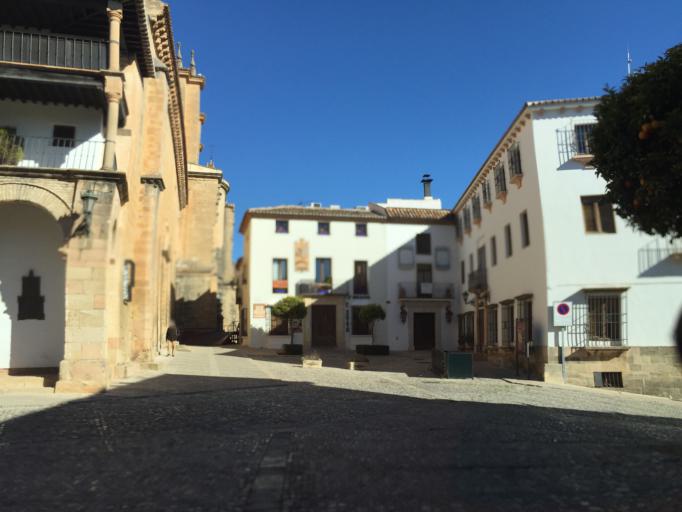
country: ES
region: Andalusia
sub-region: Provincia de Malaga
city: Ronda
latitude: 36.7372
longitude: -5.1651
